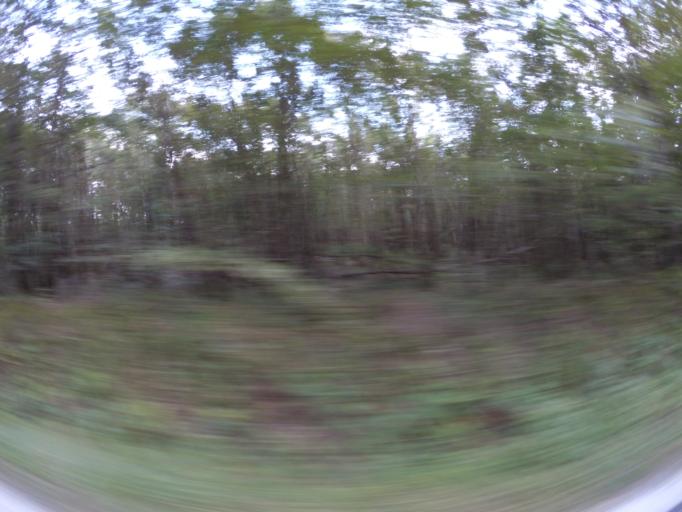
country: FR
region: Centre
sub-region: Departement d'Indre-et-Loire
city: Nazelles-Negron
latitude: 47.4592
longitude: 0.9547
